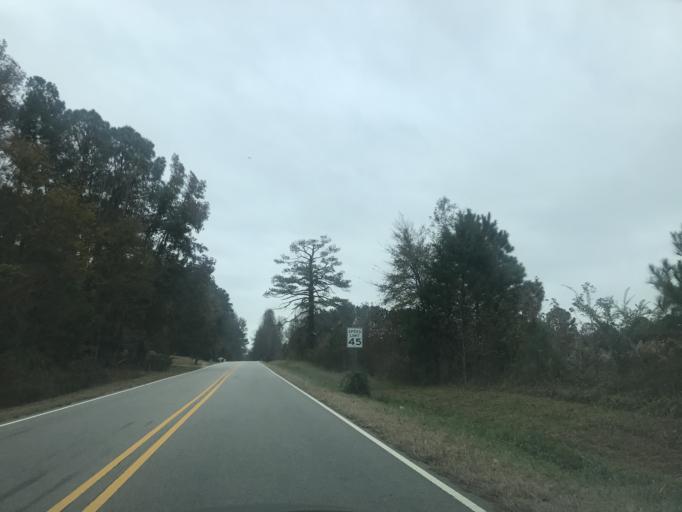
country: US
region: North Carolina
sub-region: Wake County
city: Wake Forest
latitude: 36.0009
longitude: -78.4949
